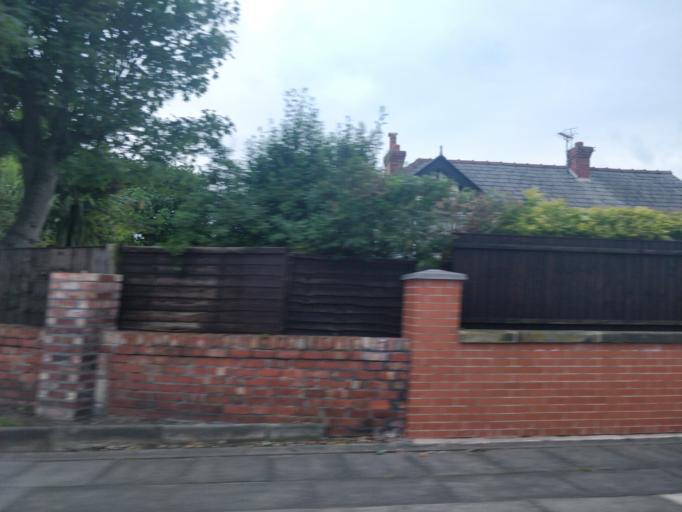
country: GB
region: England
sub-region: Sefton
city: Southport
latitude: 53.6707
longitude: -2.9738
